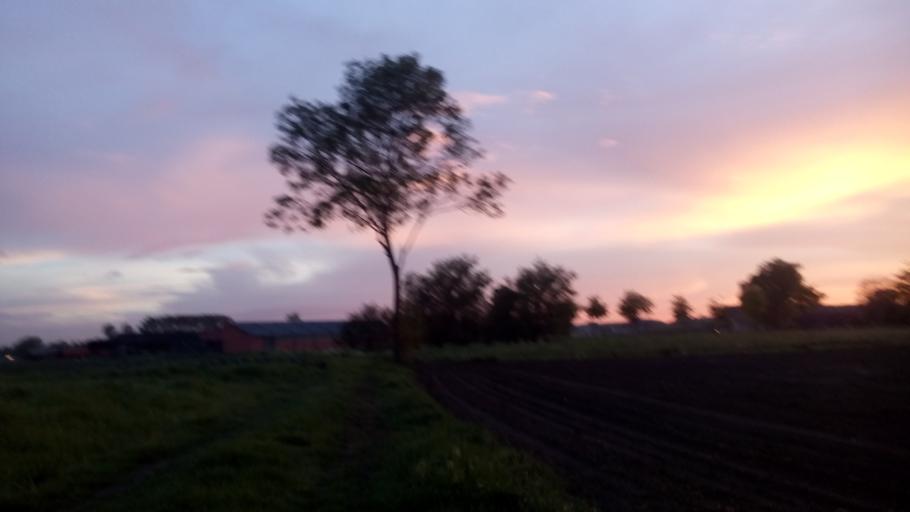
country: BE
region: Flanders
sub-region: Provincie Oost-Vlaanderen
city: Nevele
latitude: 51.0661
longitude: 3.5381
